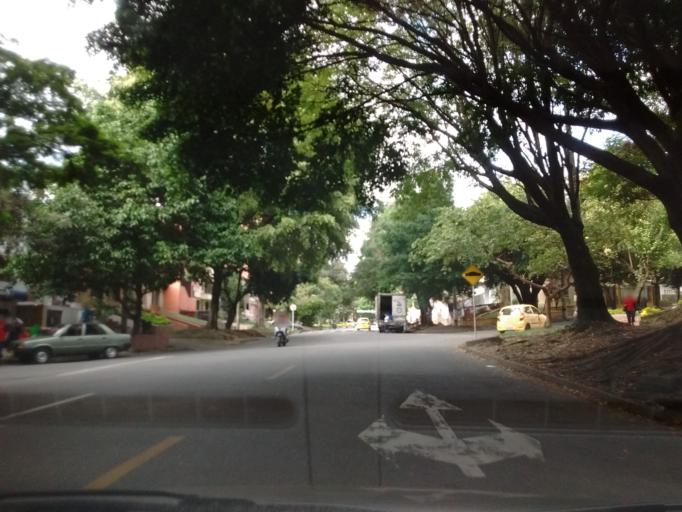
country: CO
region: Antioquia
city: Medellin
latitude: 6.2482
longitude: -75.6053
